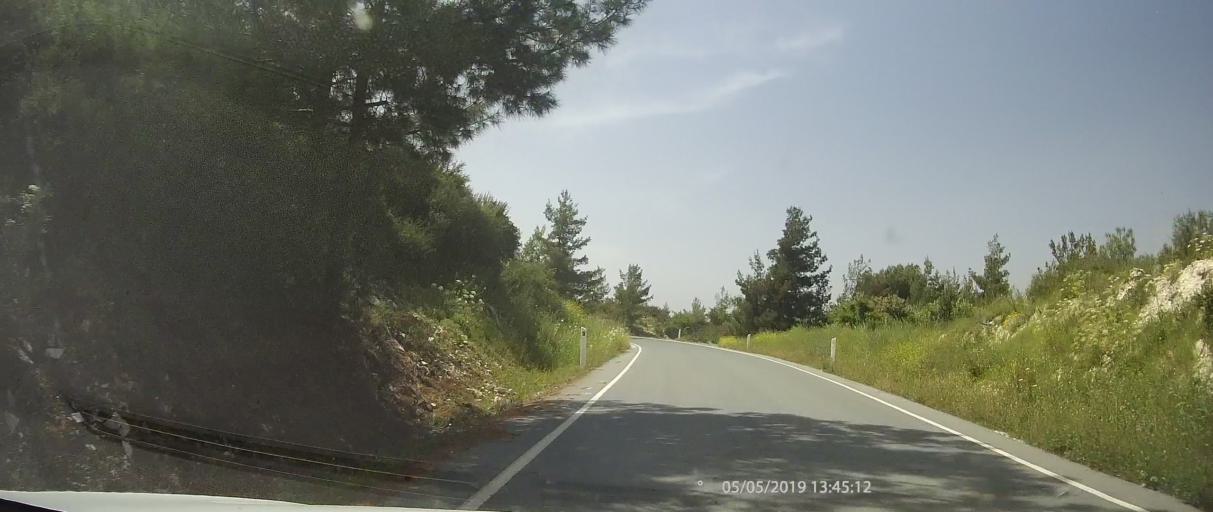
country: CY
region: Limassol
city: Pachna
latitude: 34.8700
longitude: 32.7841
